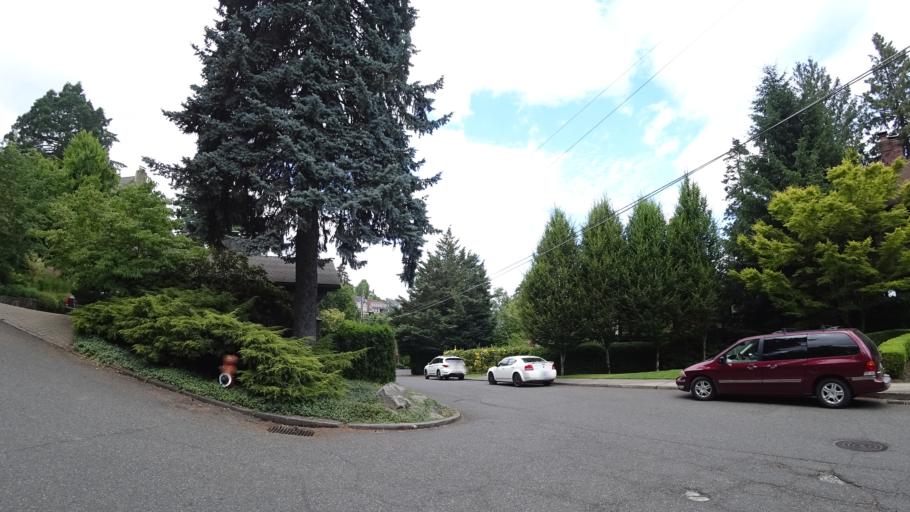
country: US
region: Oregon
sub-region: Multnomah County
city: Portland
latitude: 45.5274
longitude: -122.7053
